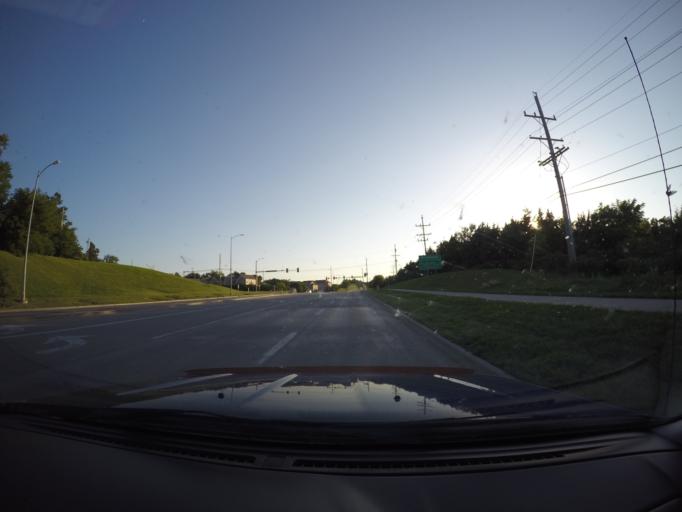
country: US
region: Kansas
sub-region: Riley County
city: Manhattan
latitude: 39.2068
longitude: -96.5751
